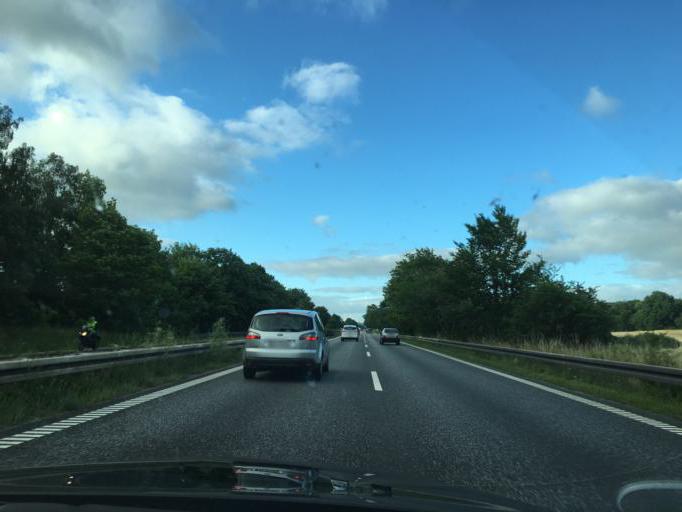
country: DK
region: Capital Region
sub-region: Fredensborg Kommune
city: Kokkedal
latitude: 55.9011
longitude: 12.4736
